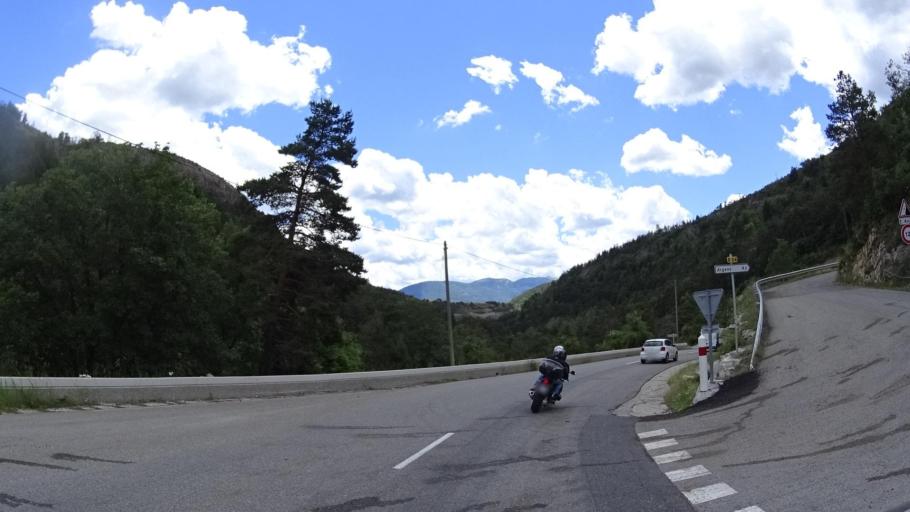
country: FR
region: Provence-Alpes-Cote d'Azur
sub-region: Departement des Alpes-de-Haute-Provence
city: Annot
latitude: 44.0222
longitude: 6.5556
